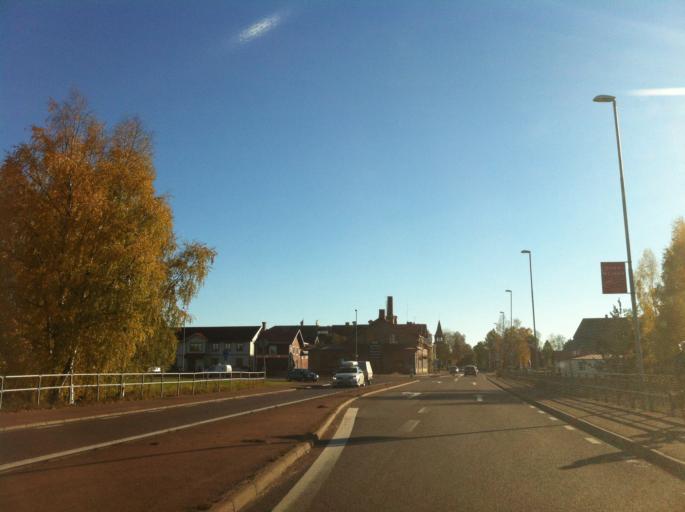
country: SE
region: Dalarna
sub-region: Mora Kommun
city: Mora
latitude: 61.0101
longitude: 14.5415
